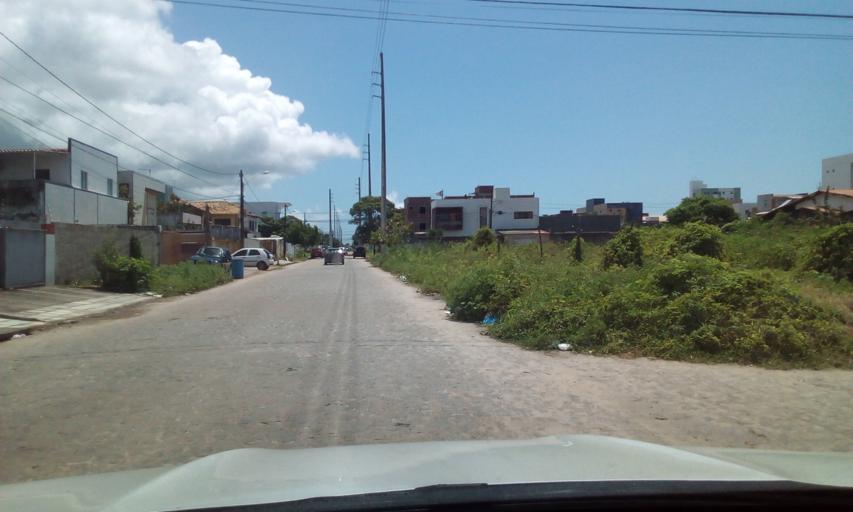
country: BR
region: Paraiba
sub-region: Joao Pessoa
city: Joao Pessoa
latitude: -7.0700
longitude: -34.8459
